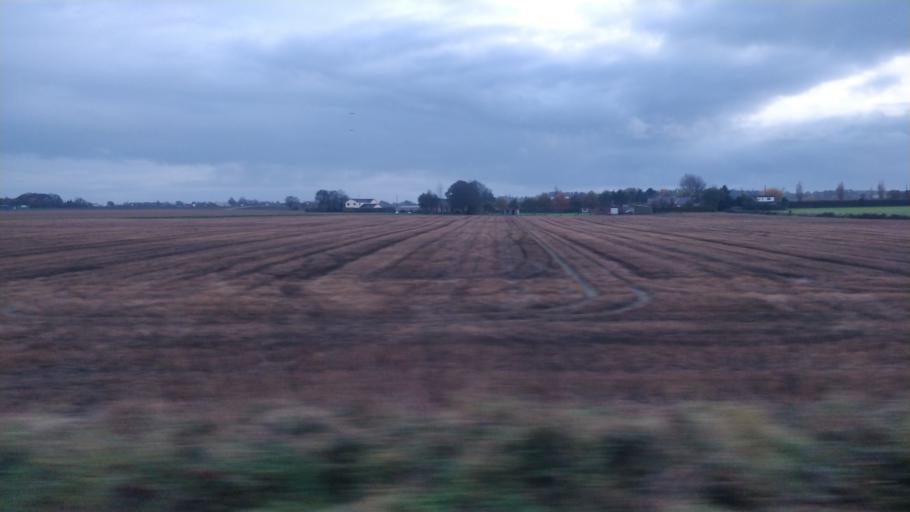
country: GB
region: England
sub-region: Lancashire
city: Ormskirk
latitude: 53.6193
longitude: -2.8966
